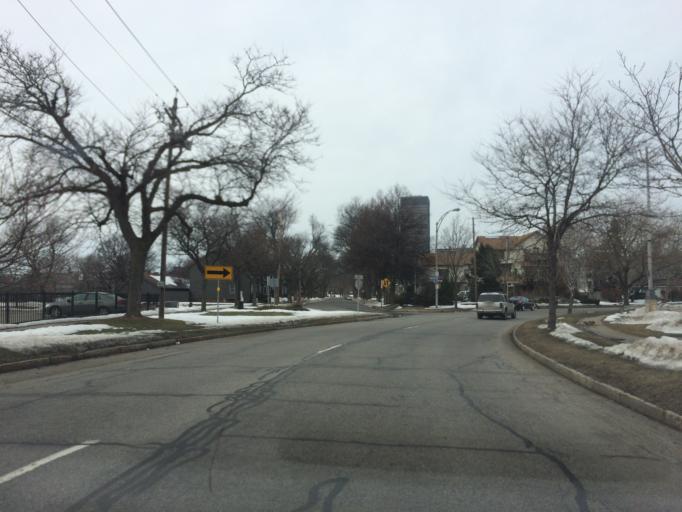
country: US
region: New York
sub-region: Monroe County
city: Rochester
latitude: 43.1475
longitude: -77.6007
